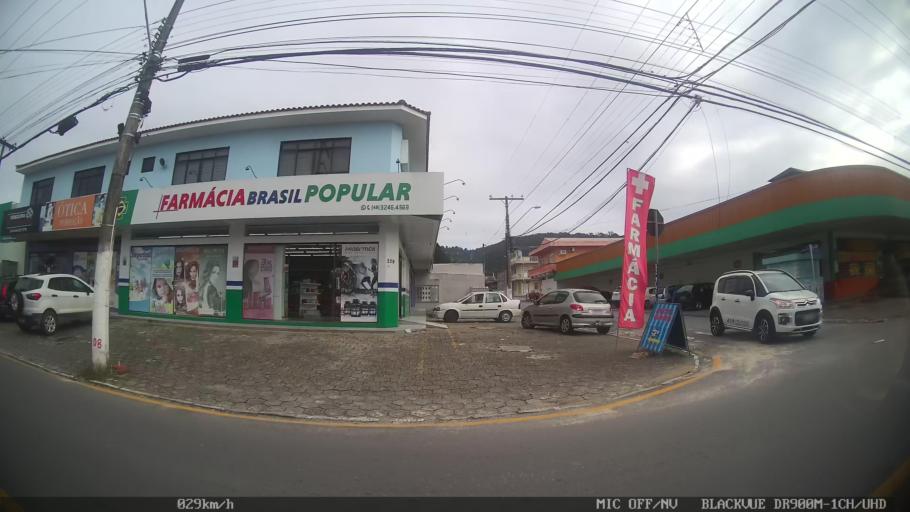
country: BR
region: Santa Catarina
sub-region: Sao Jose
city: Campinas
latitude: -27.5759
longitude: -48.6225
